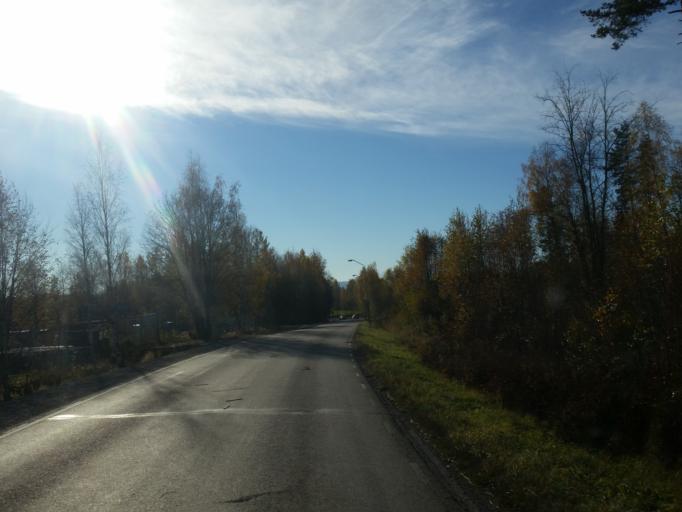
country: SE
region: Dalarna
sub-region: Borlange Kommun
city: Ornas
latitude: 60.5075
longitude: 15.5214
